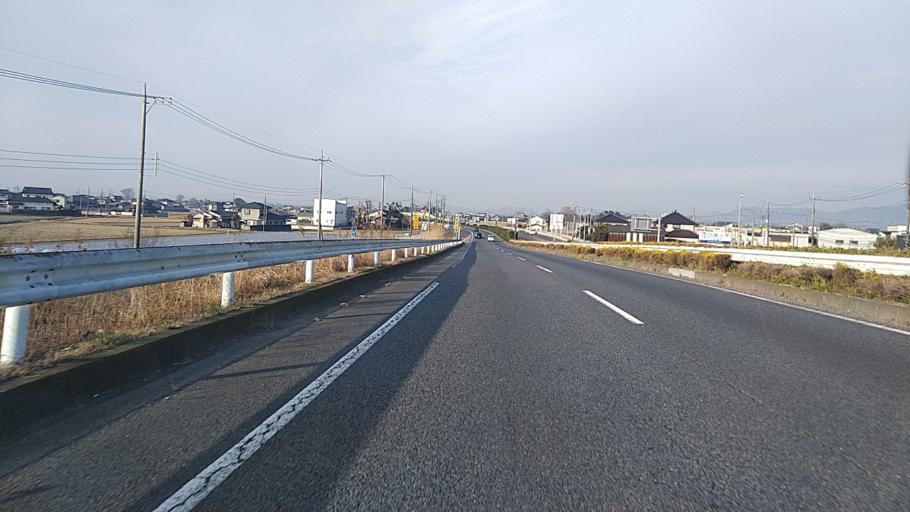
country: JP
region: Tochigi
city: Oyama
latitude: 36.3105
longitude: 139.7808
